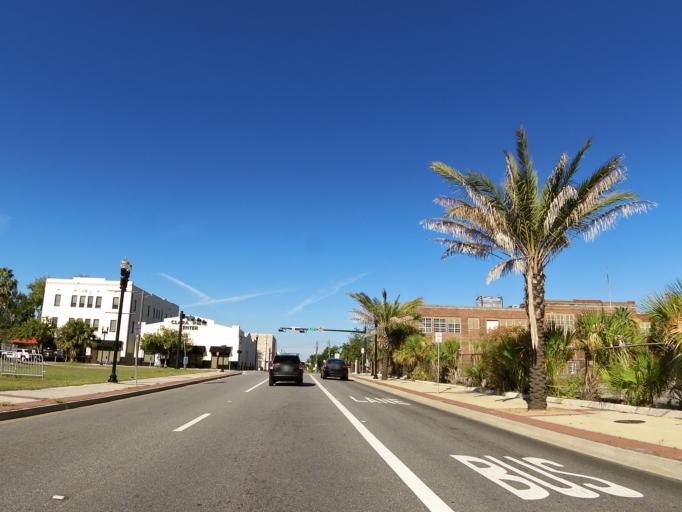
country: US
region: Florida
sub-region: Duval County
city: Jacksonville
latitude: 30.3318
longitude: -81.6642
